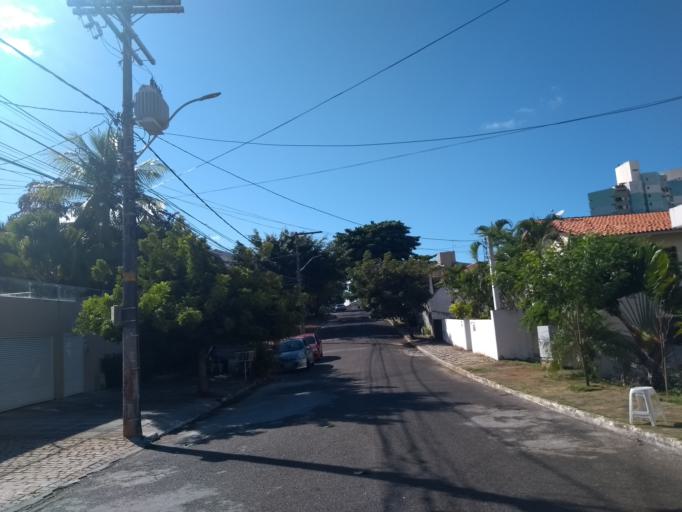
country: BR
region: Bahia
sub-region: Salvador
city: Salvador
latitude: -12.9954
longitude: -38.4622
